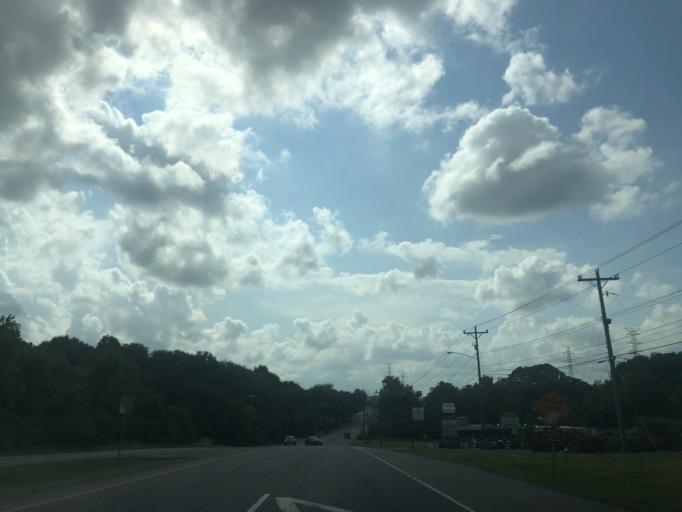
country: US
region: Tennessee
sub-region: Davidson County
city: Lakewood
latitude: 36.1571
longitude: -86.6335
